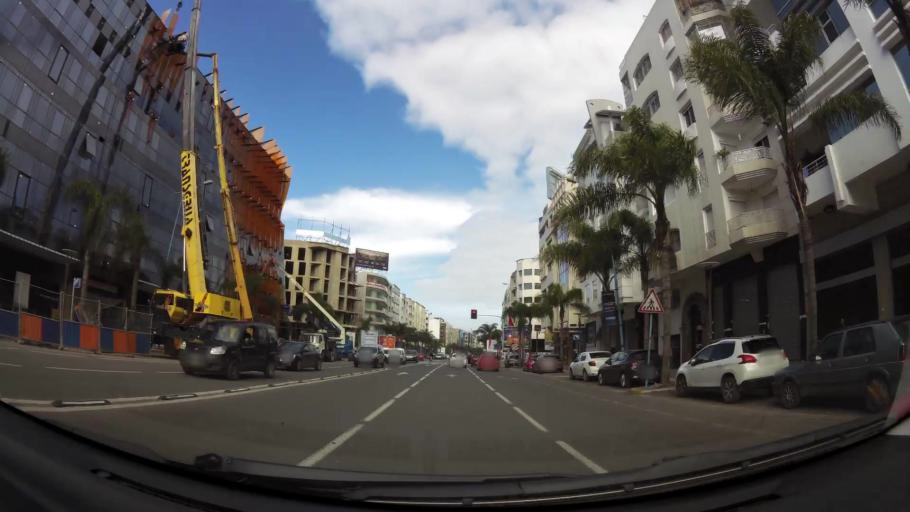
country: MA
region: Grand Casablanca
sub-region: Casablanca
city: Casablanca
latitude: 33.5869
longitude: -7.6386
